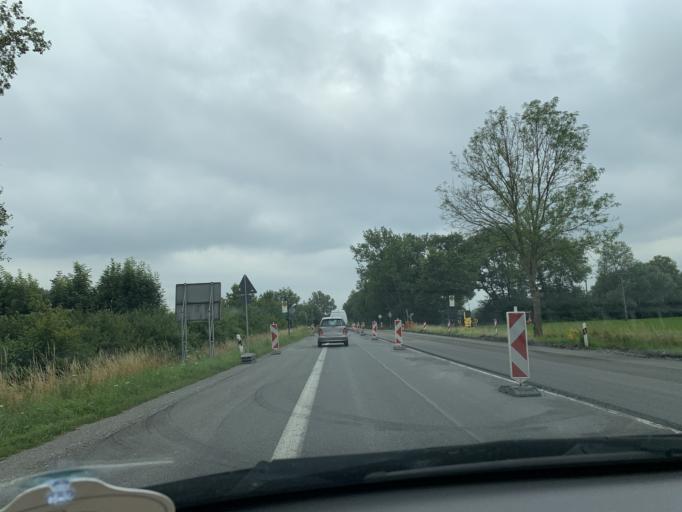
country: DE
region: North Rhine-Westphalia
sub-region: Regierungsbezirk Munster
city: Ennigerloh
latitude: 51.8987
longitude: 8.0538
